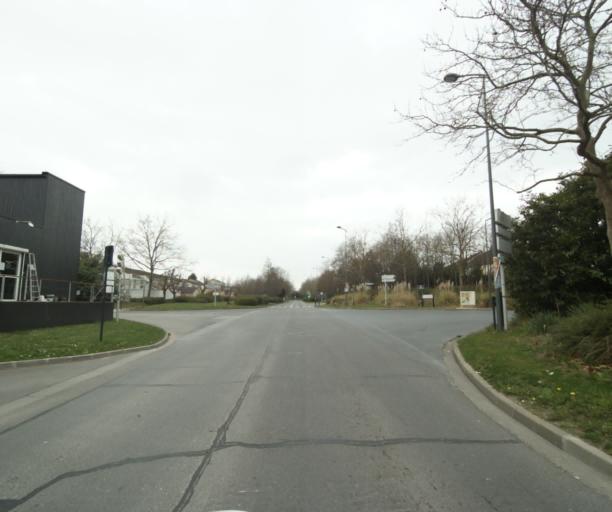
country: FR
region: Ile-de-France
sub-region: Departement du Val-d'Oise
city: Vaureal
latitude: 49.0448
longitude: 2.0267
